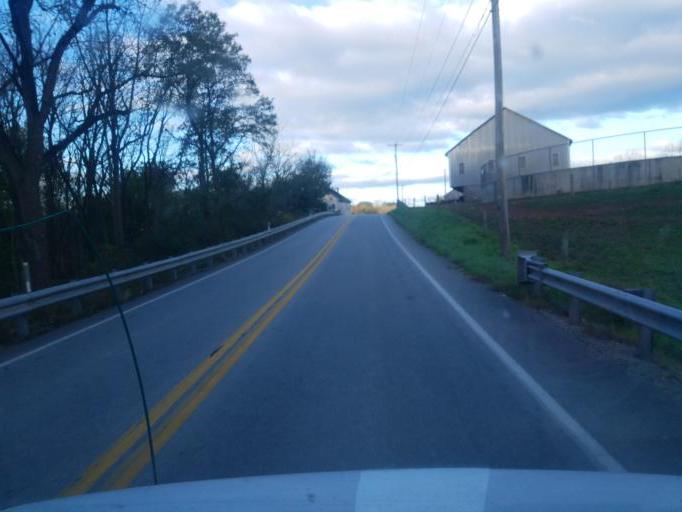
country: US
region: Pennsylvania
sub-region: Adams County
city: East Berlin
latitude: 39.9366
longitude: -77.0259
